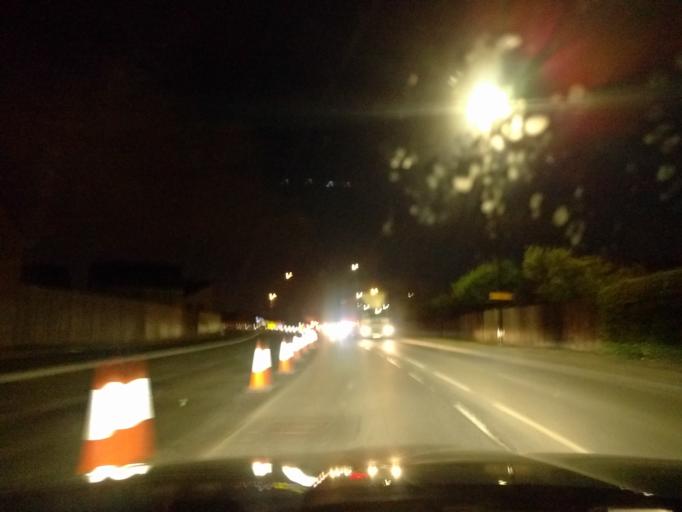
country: GB
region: England
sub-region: Northumberland
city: Backworth
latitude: 55.0267
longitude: -1.5252
